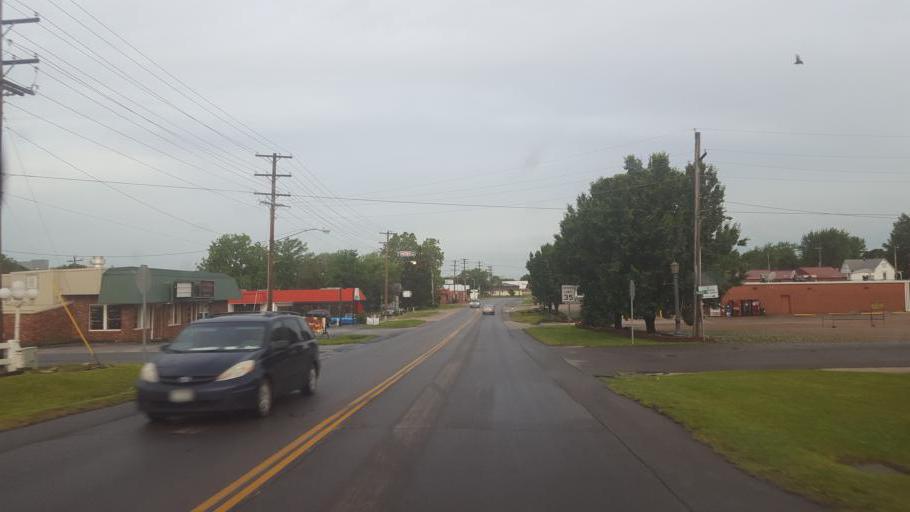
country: US
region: Missouri
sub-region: Moniteau County
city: California
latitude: 38.6277
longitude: -92.5703
